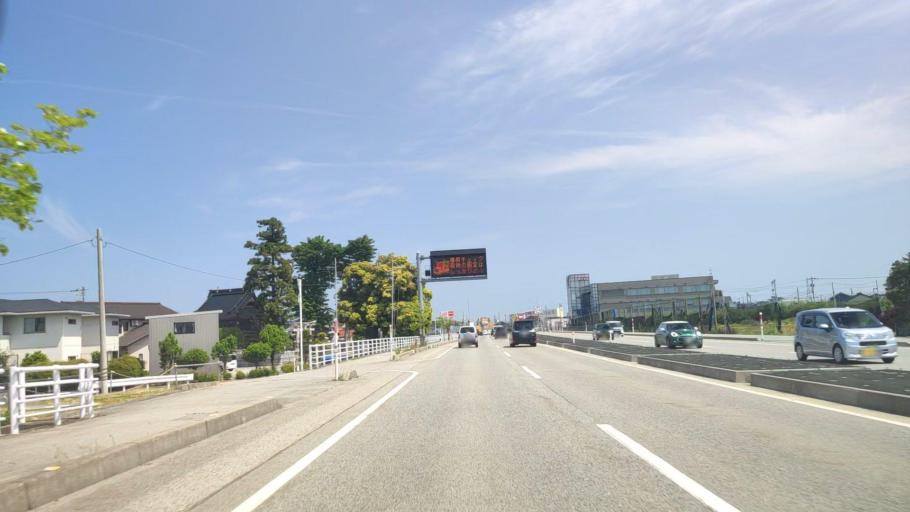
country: JP
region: Toyama
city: Uozu
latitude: 36.8289
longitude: 137.4188
